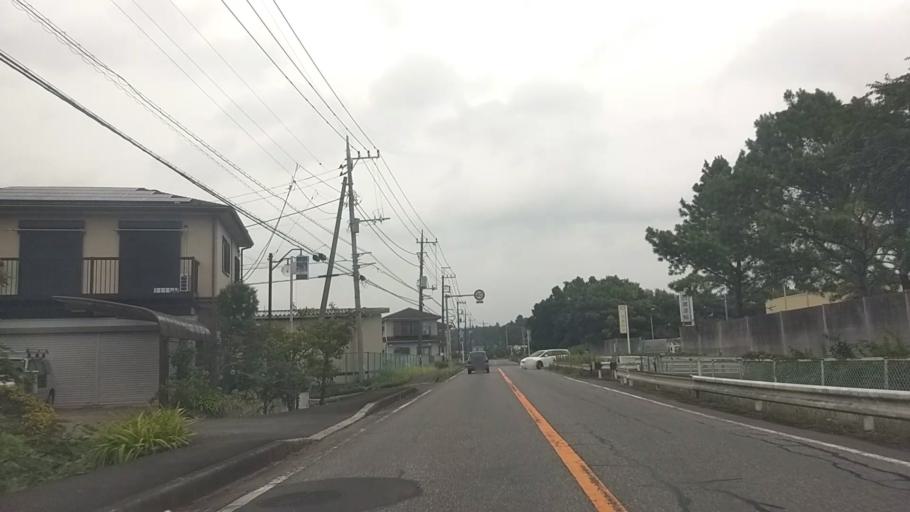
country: JP
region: Chiba
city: Kisarazu
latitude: 35.3871
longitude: 140.0453
